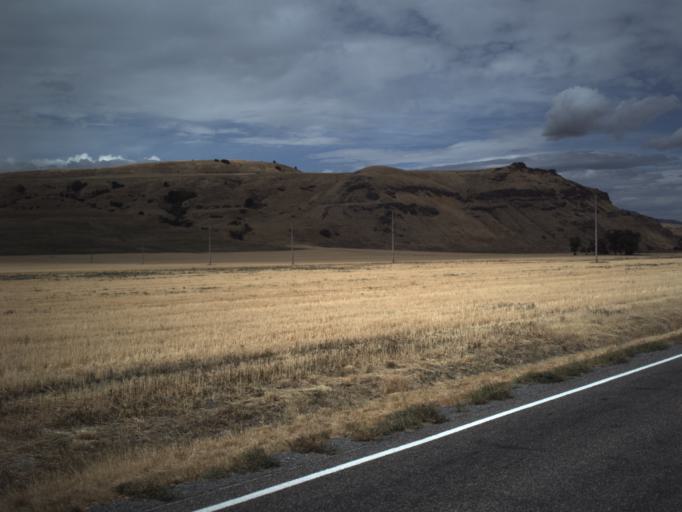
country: US
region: Utah
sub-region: Cache County
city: Benson
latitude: 41.7821
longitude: -111.9859
